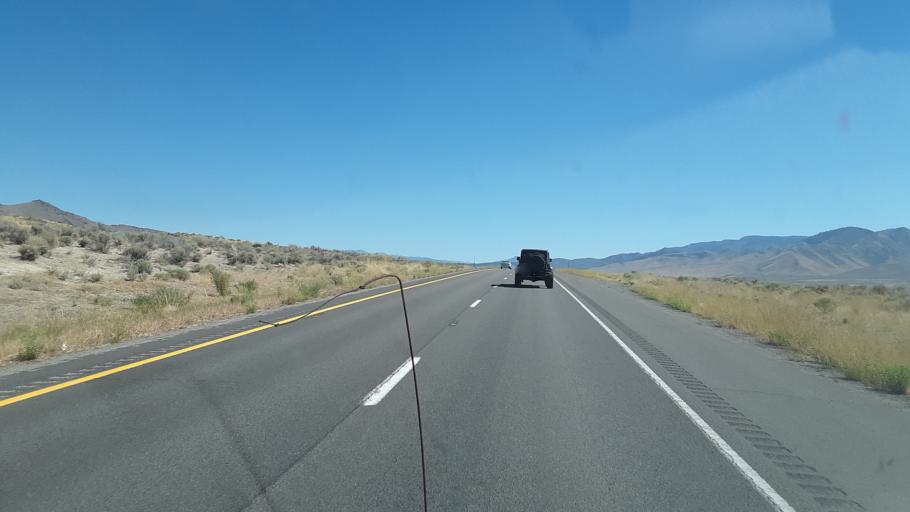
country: US
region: Nevada
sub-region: Washoe County
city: Cold Springs
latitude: 39.7618
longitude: -120.0391
